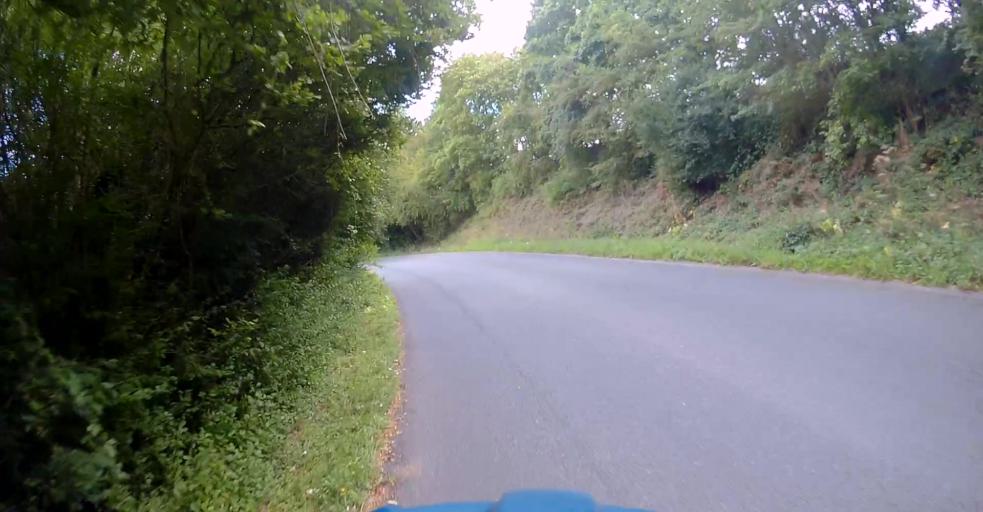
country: GB
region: England
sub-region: Hampshire
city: Basingstoke
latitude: 51.2371
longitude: -1.1072
